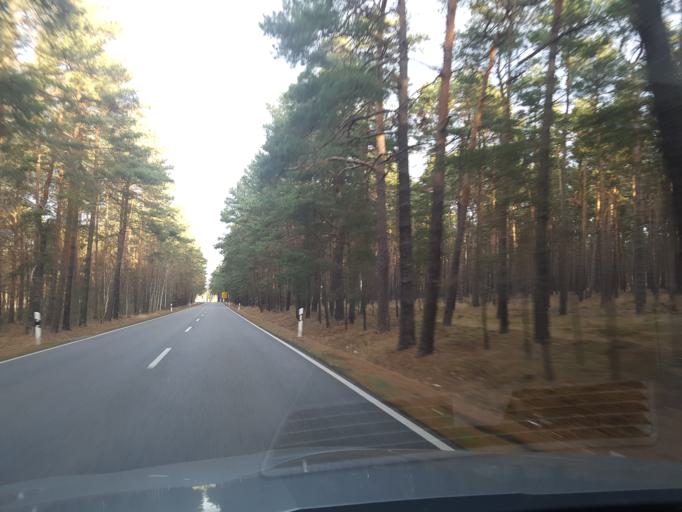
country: DE
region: Brandenburg
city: Kasel-Golzig
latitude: 51.9228
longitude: 13.6667
